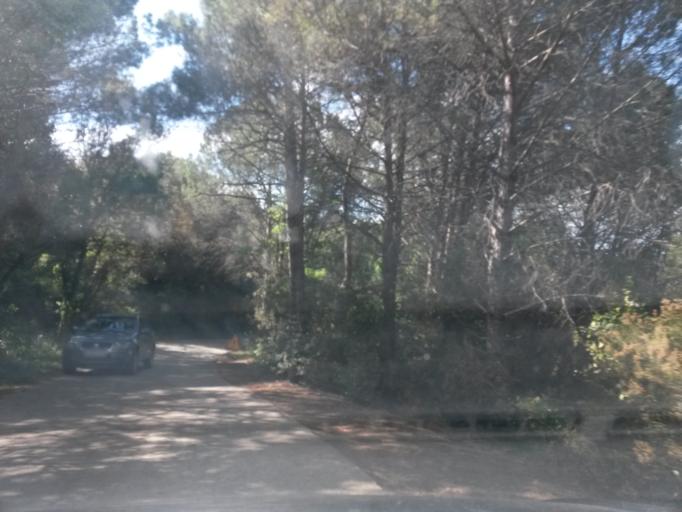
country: ES
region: Catalonia
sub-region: Provincia de Girona
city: Brunyola
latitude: 41.9056
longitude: 2.6873
